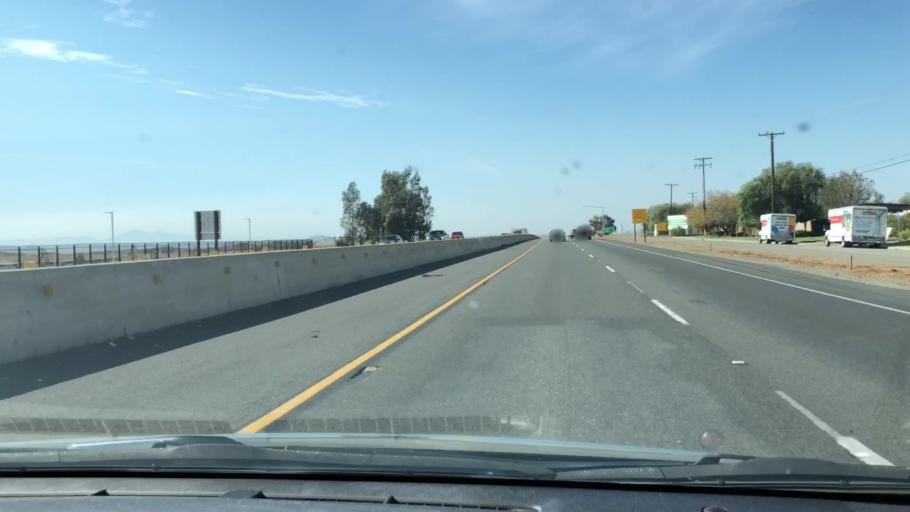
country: US
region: California
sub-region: Riverside County
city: Beaumont
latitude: 33.9336
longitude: -117.0022
